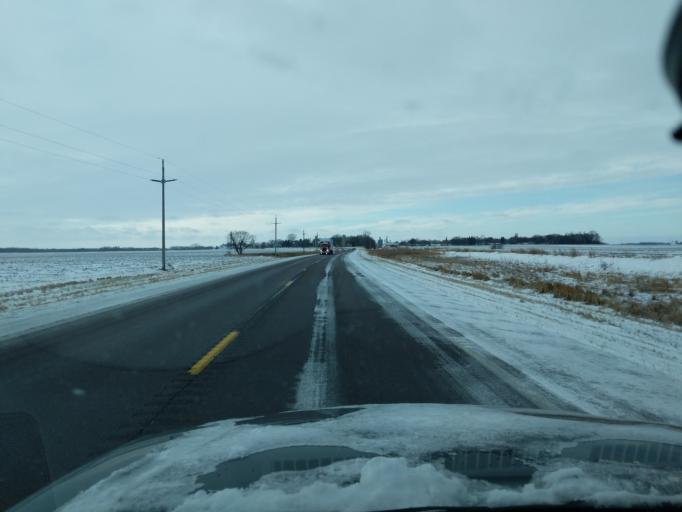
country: US
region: Minnesota
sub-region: McLeod County
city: Hutchinson
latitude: 44.7219
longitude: -94.4647
